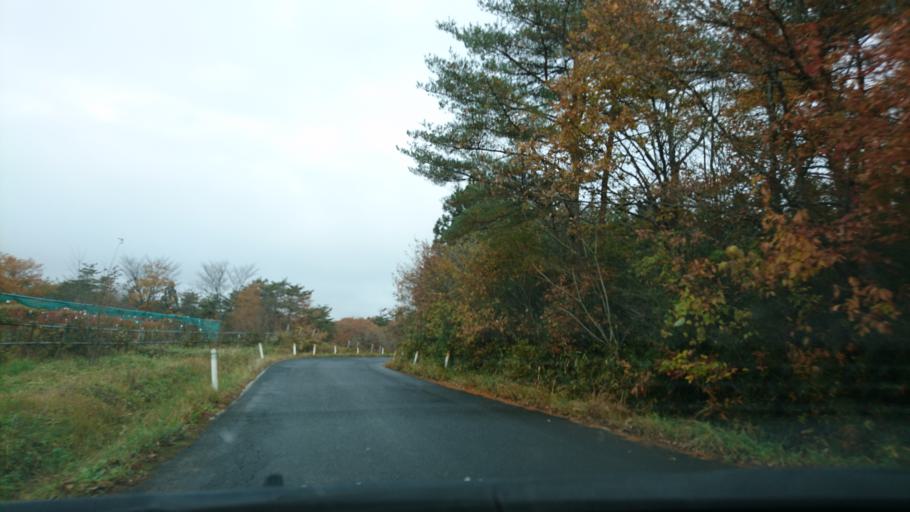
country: JP
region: Iwate
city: Ichinoseki
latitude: 38.8824
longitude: 141.1732
